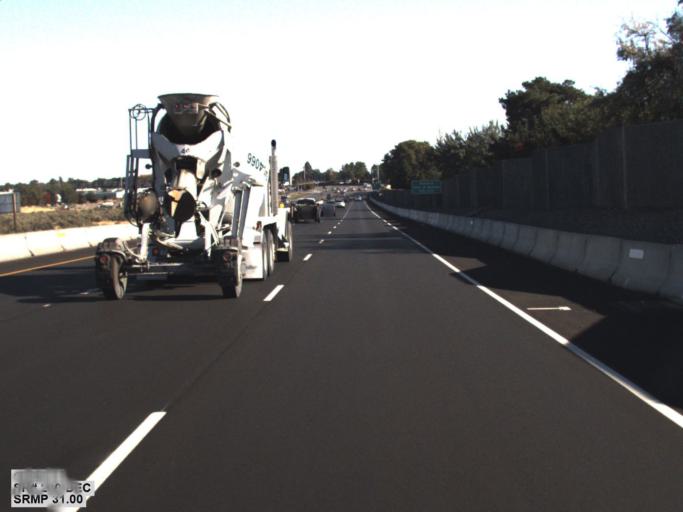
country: US
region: Washington
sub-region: Benton County
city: Richland
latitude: 46.3047
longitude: -119.2911
